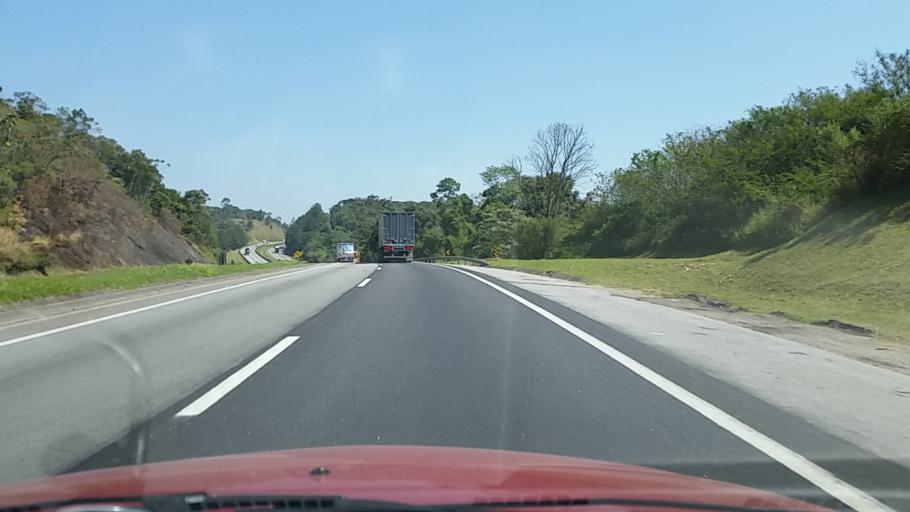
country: BR
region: Sao Paulo
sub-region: Juquitiba
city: Juquitiba
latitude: -23.9597
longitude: -47.1183
